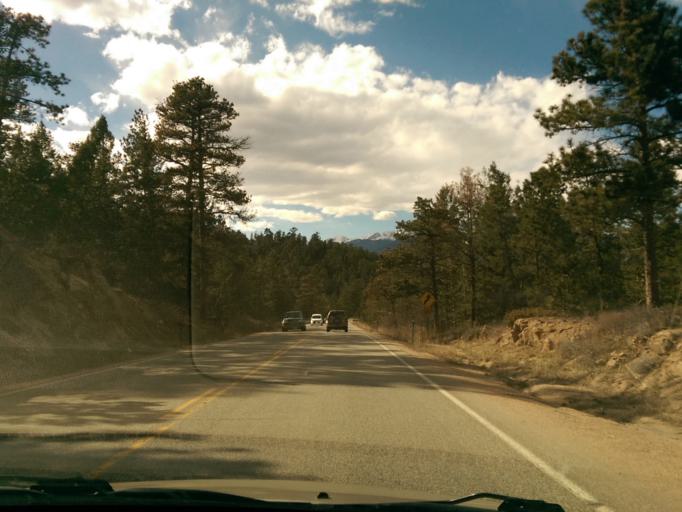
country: US
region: Colorado
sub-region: Larimer County
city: Estes Park
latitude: 40.3631
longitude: -105.4693
